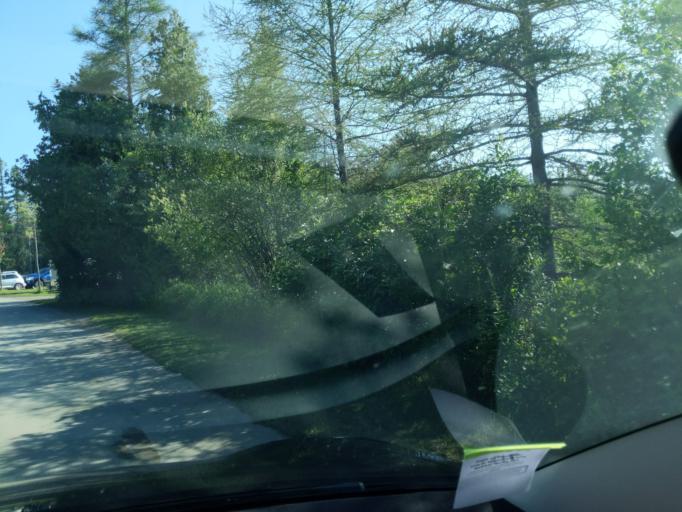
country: US
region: Michigan
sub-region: Mackinac County
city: Saint Ignace
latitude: 45.7521
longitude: -84.6823
